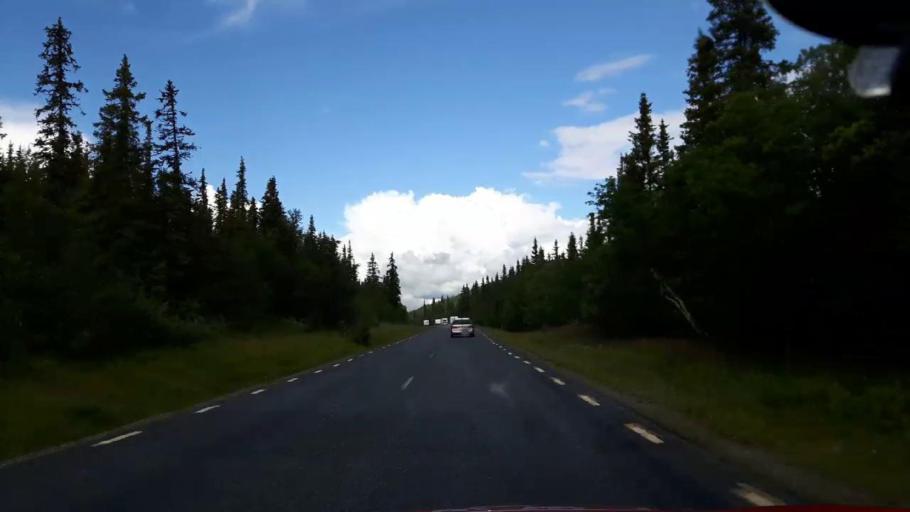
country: SE
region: Vaesterbotten
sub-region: Vilhelmina Kommun
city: Sjoberg
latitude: 65.0243
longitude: 15.1532
